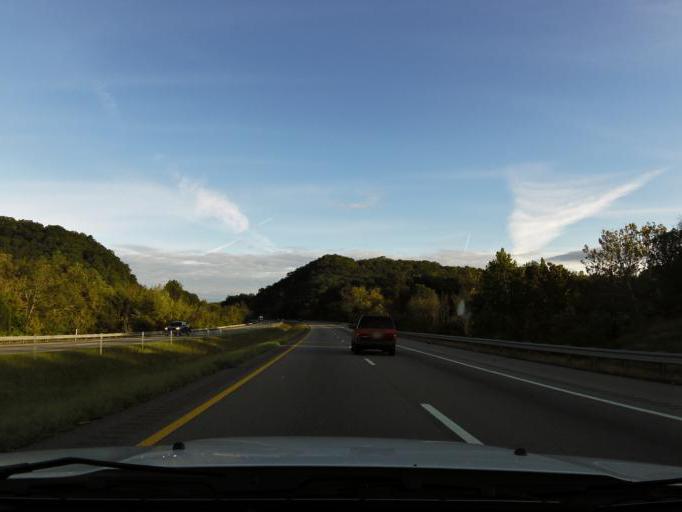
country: US
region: Tennessee
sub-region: Anderson County
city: Norris
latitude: 36.1285
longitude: -84.0362
